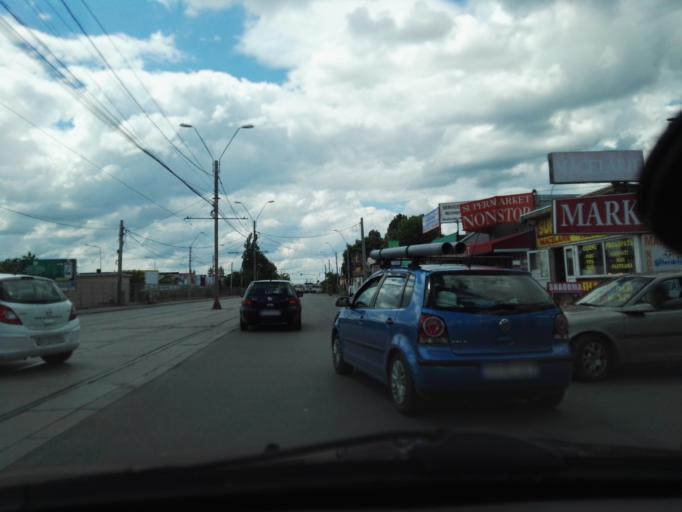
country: RO
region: Ilfov
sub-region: Comuna Jilava
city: Jilava
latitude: 44.3719
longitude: 26.0899
